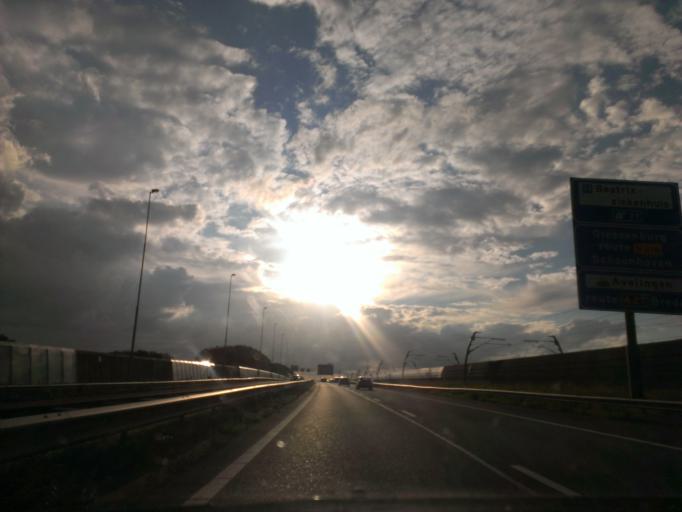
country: NL
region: South Holland
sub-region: Gemeente Gorinchem
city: Gorinchem
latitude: 51.8468
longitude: 4.9820
